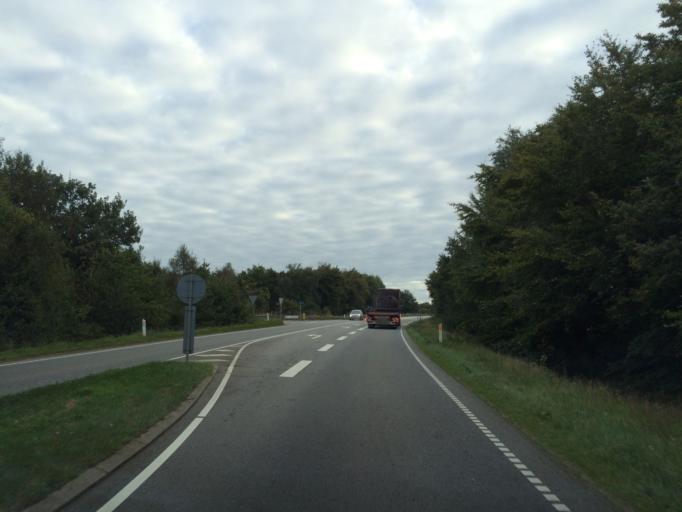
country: DK
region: Central Jutland
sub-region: Ringkobing-Skjern Kommune
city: Skjern
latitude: 55.9656
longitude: 8.5515
